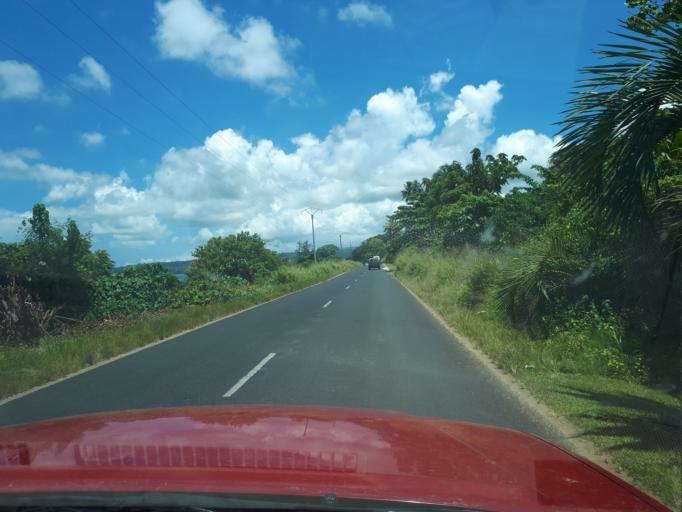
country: VU
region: Sanma
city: Luganville
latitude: -15.5154
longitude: 167.2031
